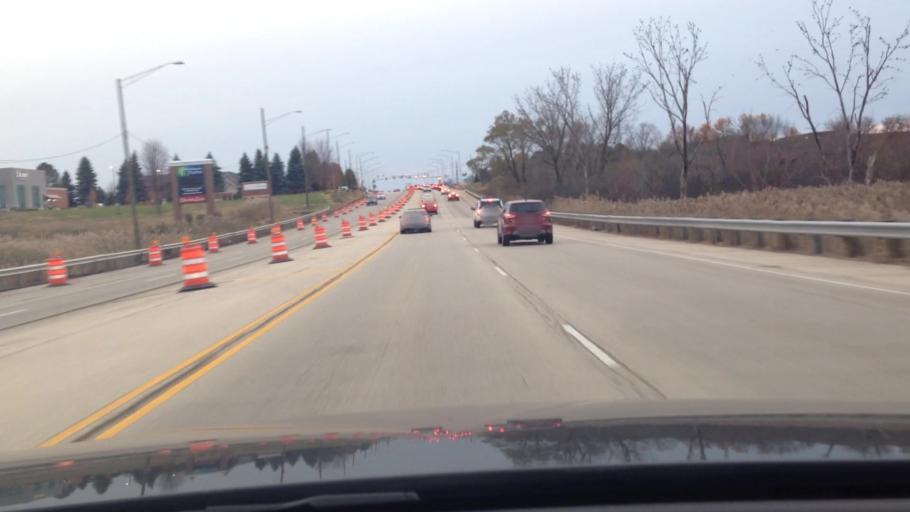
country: US
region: Illinois
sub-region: McHenry County
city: Lake in the Hills
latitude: 42.1644
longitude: -88.3354
